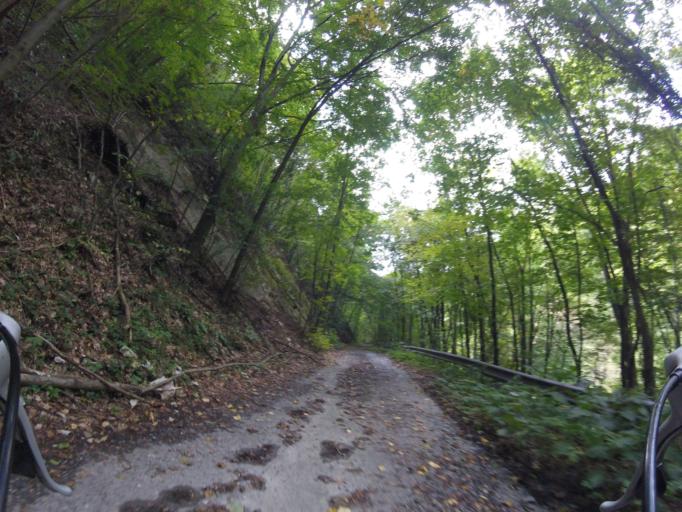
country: HU
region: Heves
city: Szilvasvarad
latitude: 48.1113
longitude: 20.5449
